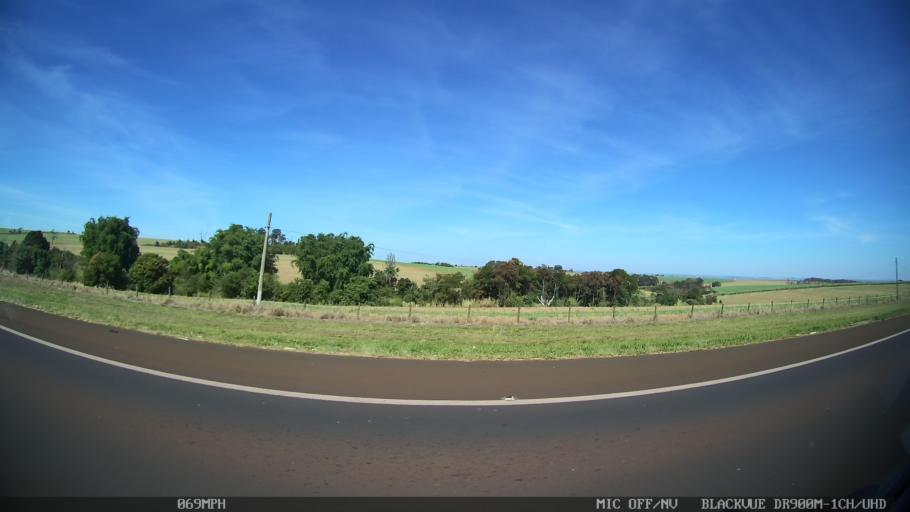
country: BR
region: Sao Paulo
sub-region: Franca
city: Franca
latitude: -20.5562
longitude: -47.5886
